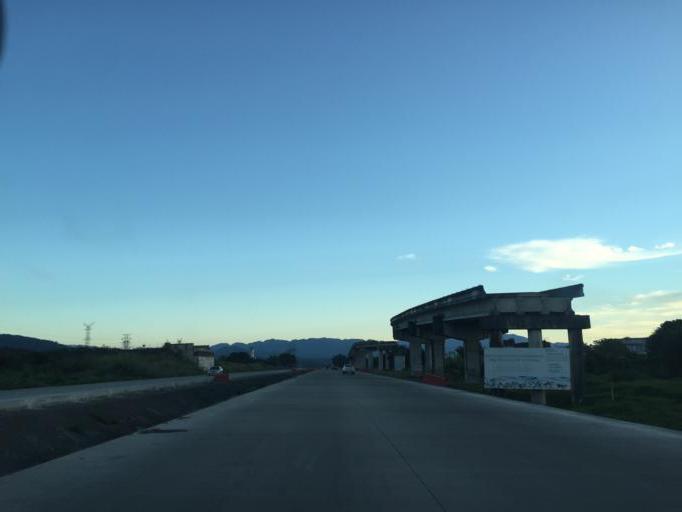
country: MX
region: Veracruz
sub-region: Ixtaczoquitlan
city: Buenavista
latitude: 18.8923
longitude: -97.0436
